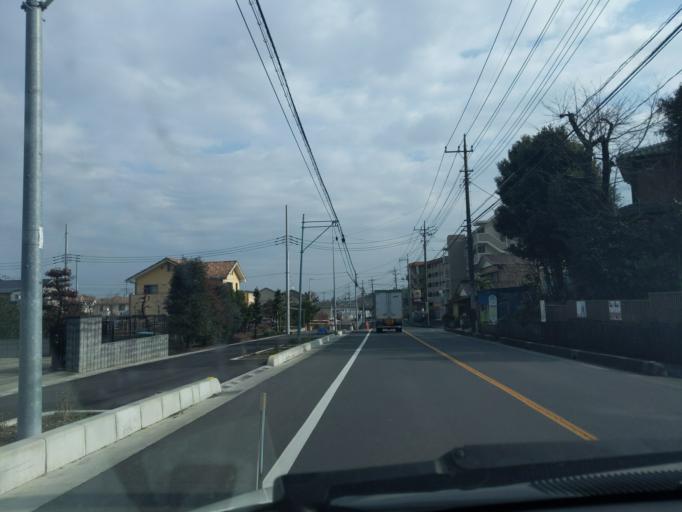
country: JP
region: Saitama
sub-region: Kawaguchi-shi
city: Hatogaya-honcho
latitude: 35.8598
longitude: 139.7439
